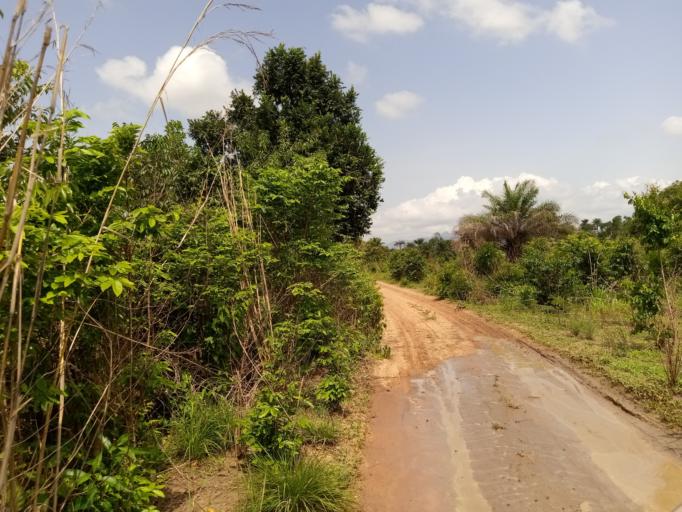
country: SL
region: Western Area
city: Waterloo
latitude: 8.3582
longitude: -13.0048
